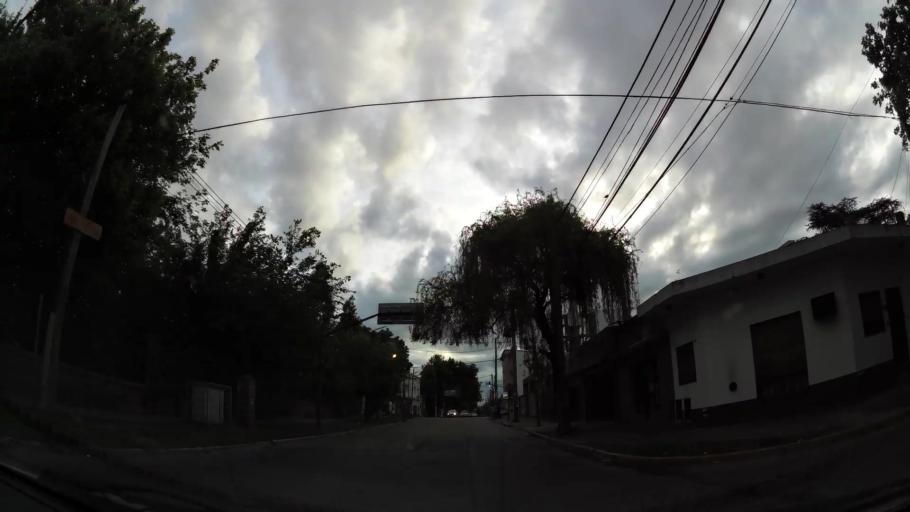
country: AR
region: Buenos Aires
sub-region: Partido de Quilmes
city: Quilmes
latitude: -34.7307
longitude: -58.2459
